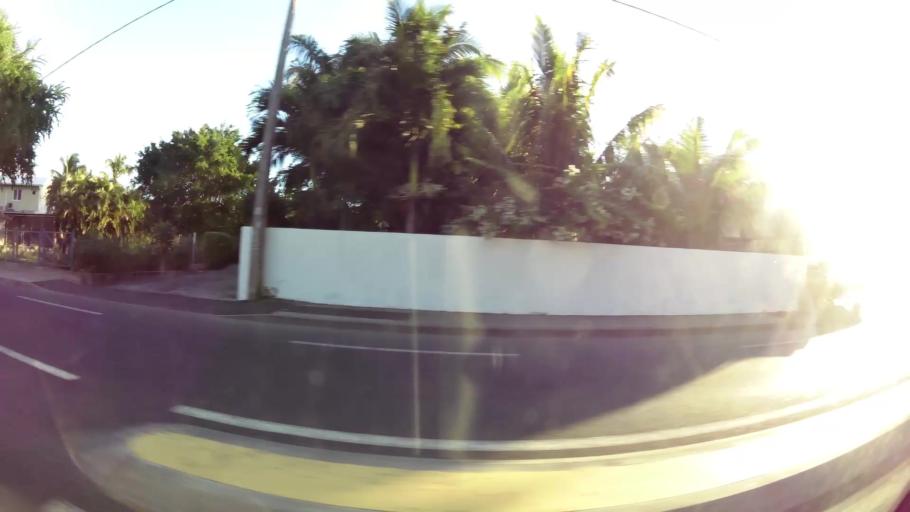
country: RE
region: Reunion
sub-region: Reunion
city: Trois-Bassins
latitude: -21.0820
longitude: 55.2304
